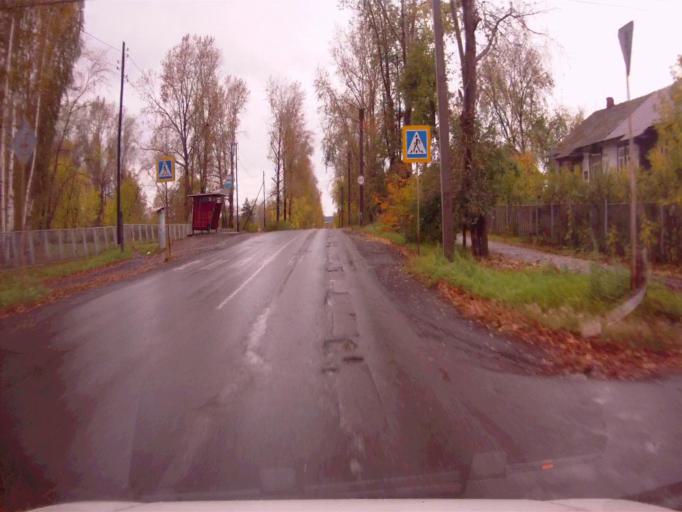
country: RU
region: Chelyabinsk
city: Verkhniy Ufaley
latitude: 56.0374
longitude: 60.2568
